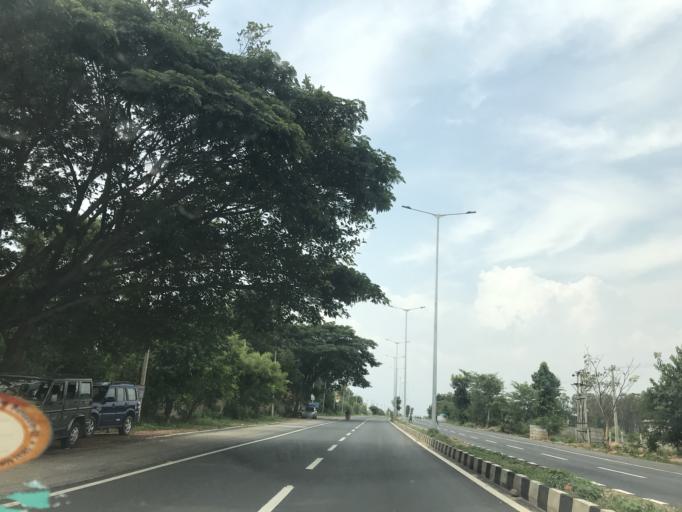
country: IN
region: Karnataka
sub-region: Bangalore Urban
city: Yelahanka
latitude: 13.1479
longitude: 77.6742
